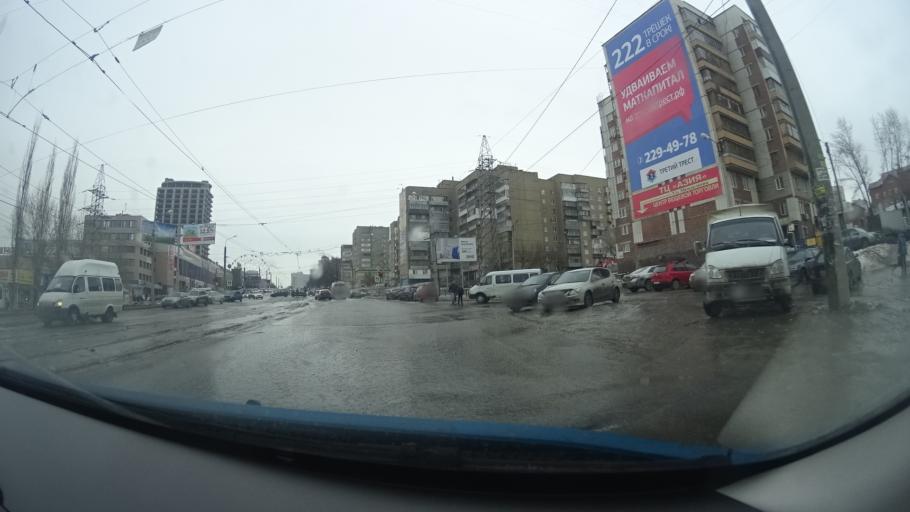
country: RU
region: Bashkortostan
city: Ufa
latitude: 54.7113
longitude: 55.9880
